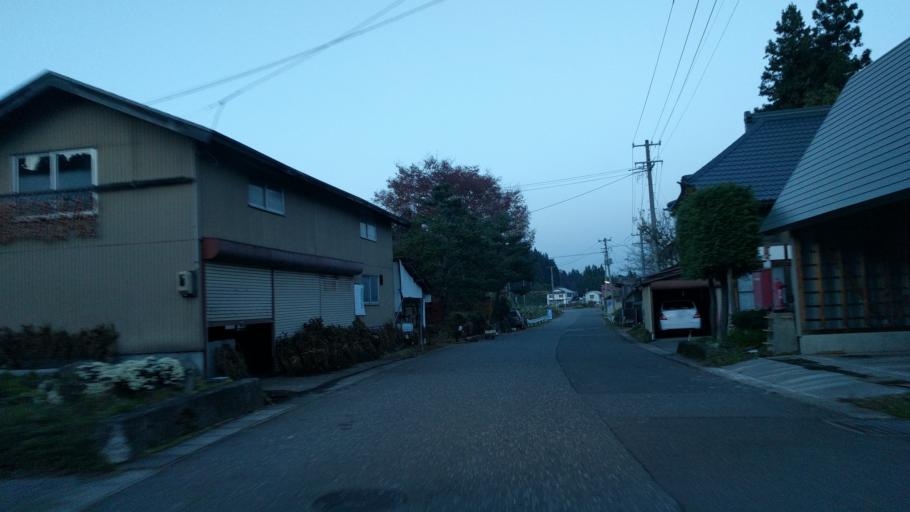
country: JP
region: Fukushima
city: Kitakata
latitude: 37.5239
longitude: 139.7113
